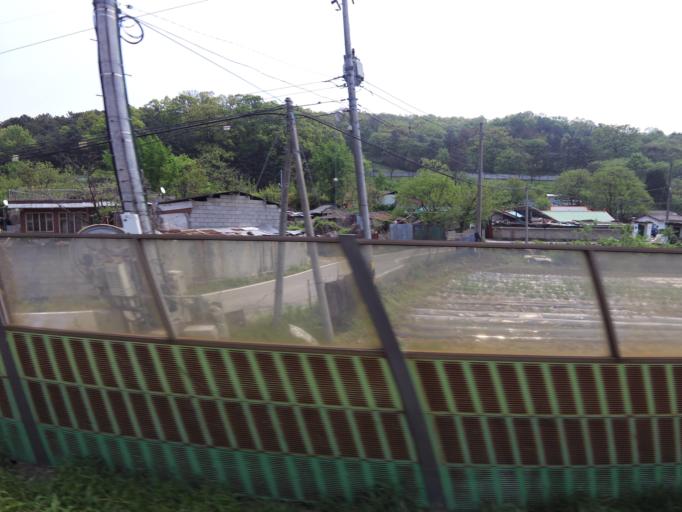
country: KR
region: Daejeon
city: Daejeon
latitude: 36.3271
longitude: 127.4751
